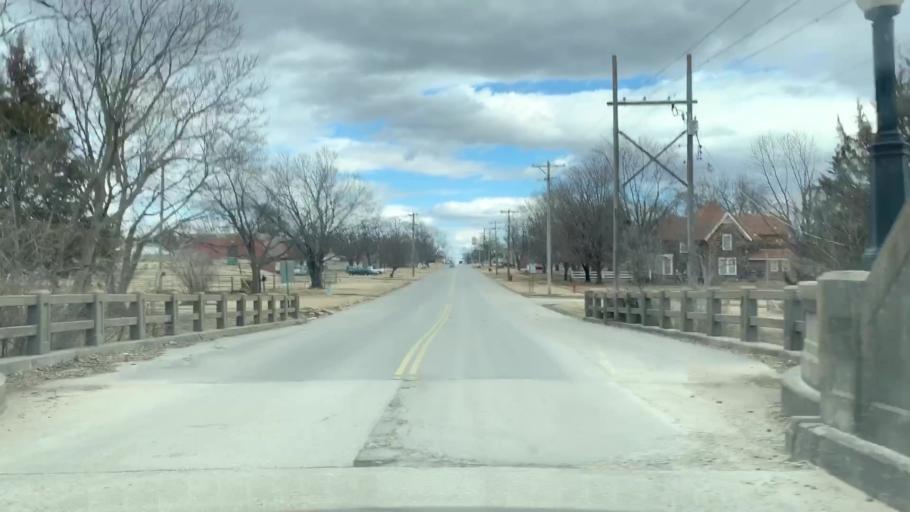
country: US
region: Kansas
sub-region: Allen County
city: Humboldt
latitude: 37.8111
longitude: -95.4474
